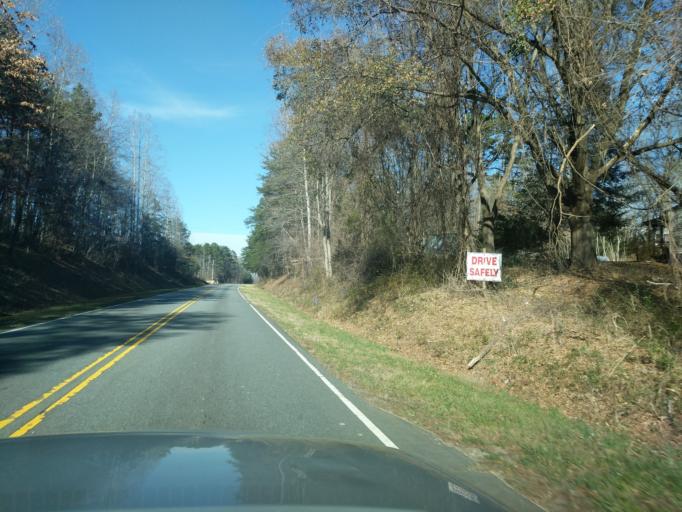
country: US
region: North Carolina
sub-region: Rutherford County
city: Rutherfordton
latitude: 35.4278
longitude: -81.9807
